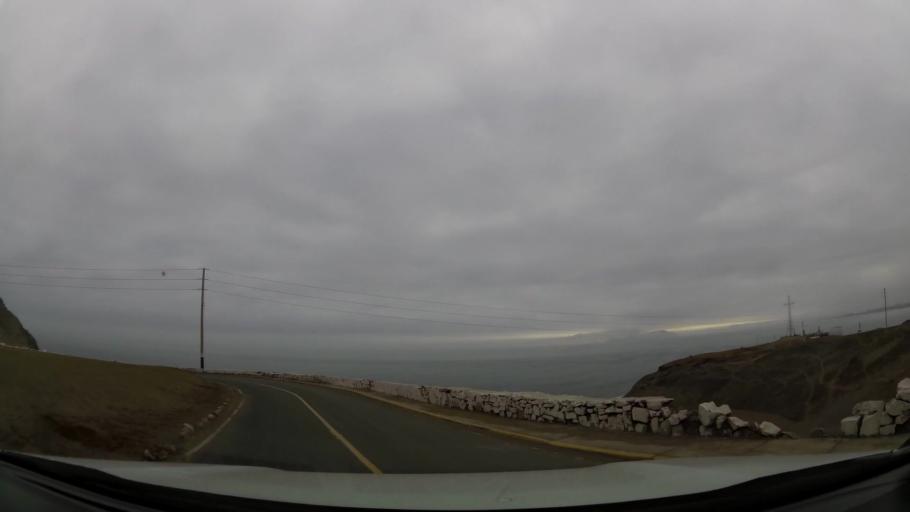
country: PE
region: Lima
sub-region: Lima
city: Surco
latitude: -12.1716
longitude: -77.0314
